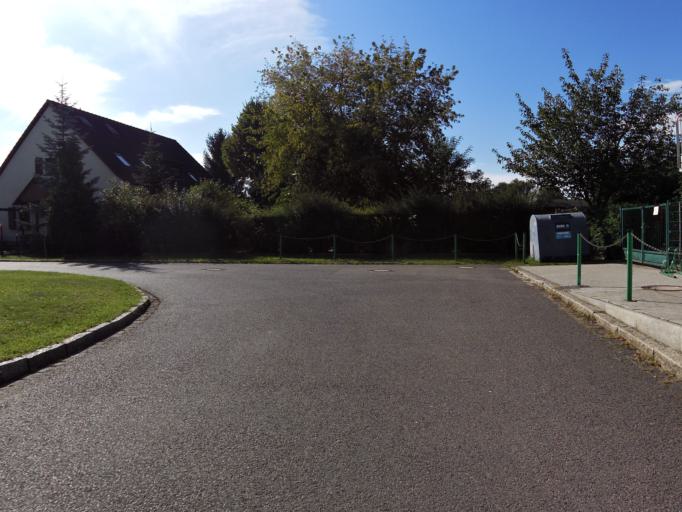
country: DE
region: Saxony-Anhalt
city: Wittenburg
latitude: 51.8670
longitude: 12.5879
